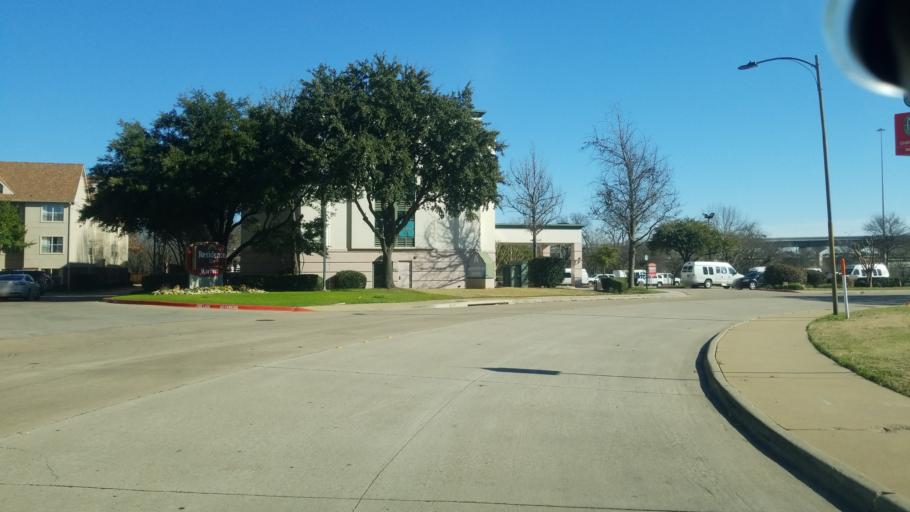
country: US
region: Texas
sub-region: Tarrant County
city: Arlington
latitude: 32.7635
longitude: -97.0667
